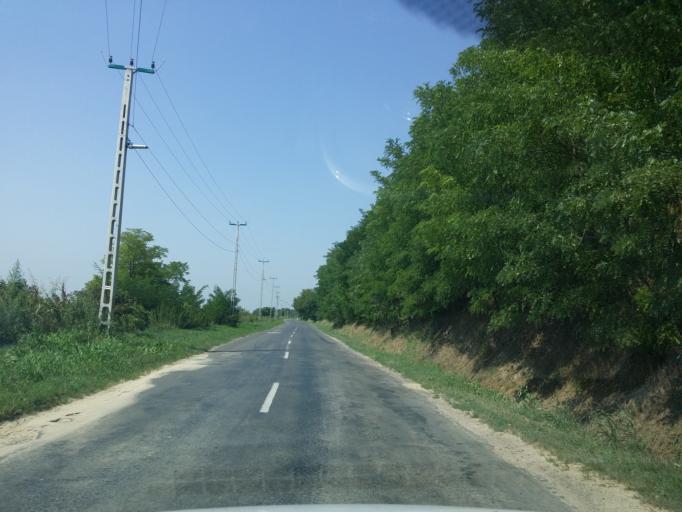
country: HU
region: Tolna
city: Gyonk
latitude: 46.6028
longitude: 18.4244
